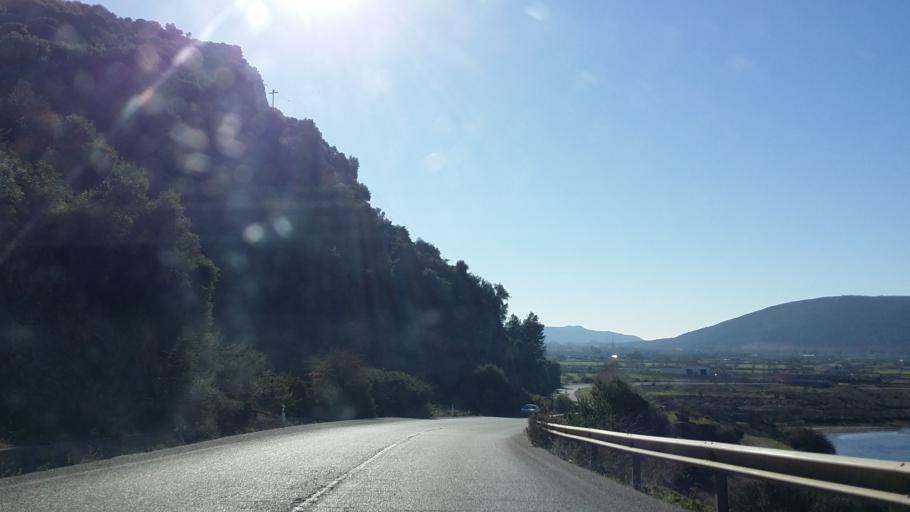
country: GR
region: West Greece
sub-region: Nomos Aitolias kai Akarnanias
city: Vonitsa
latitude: 38.9239
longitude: 20.9086
